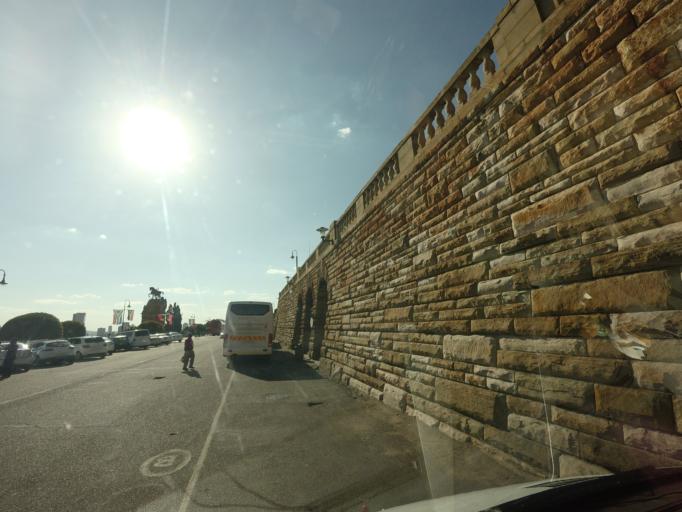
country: ZA
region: Gauteng
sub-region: City of Tshwane Metropolitan Municipality
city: Pretoria
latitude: -25.7413
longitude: 28.2125
